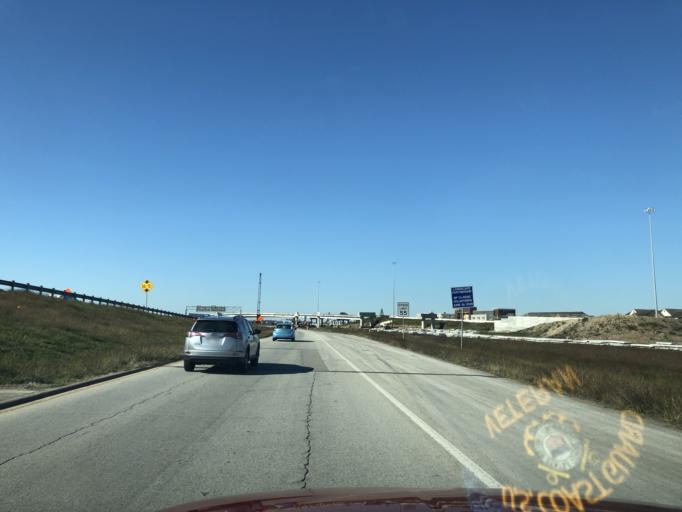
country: US
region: Texas
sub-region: Galveston County
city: Hitchcock
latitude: 29.4039
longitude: -95.0337
